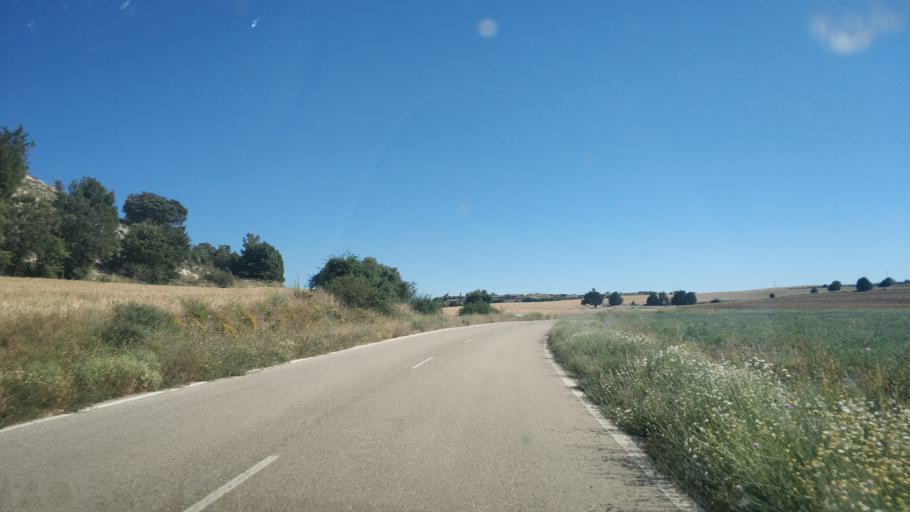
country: ES
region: Castille and Leon
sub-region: Provincia de Soria
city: Liceras
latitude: 41.4743
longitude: -3.2150
